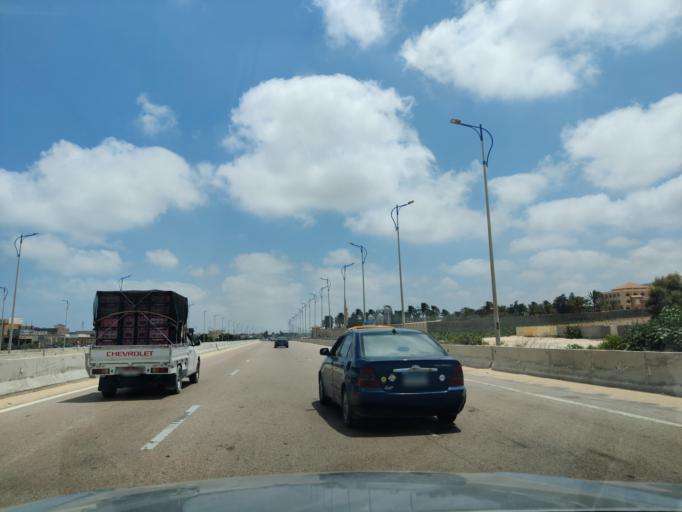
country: EG
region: Alexandria
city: Alexandria
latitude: 30.9832
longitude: 29.5821
